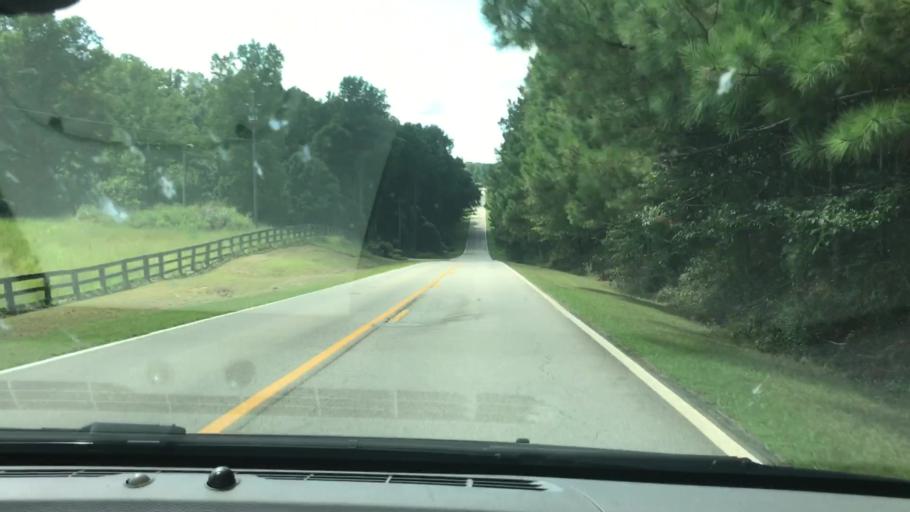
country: US
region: Georgia
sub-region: Troup County
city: La Grange
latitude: 33.1415
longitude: -85.0949
